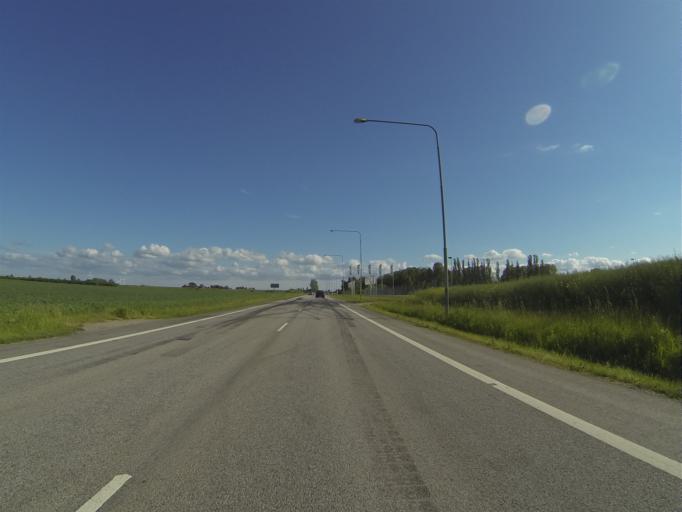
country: SE
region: Skane
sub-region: Staffanstorps Kommun
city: Staffanstorp
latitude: 55.6463
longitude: 13.2380
